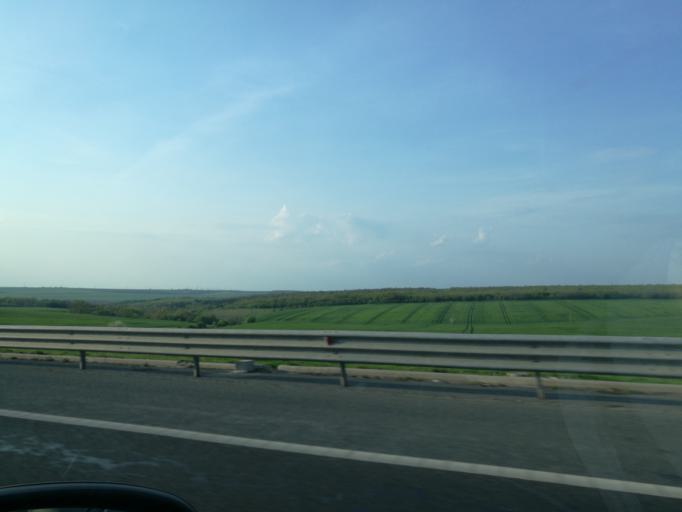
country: RO
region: Constanta
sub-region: Oras Murfatlar
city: Siminoc
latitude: 44.1351
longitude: 28.3845
